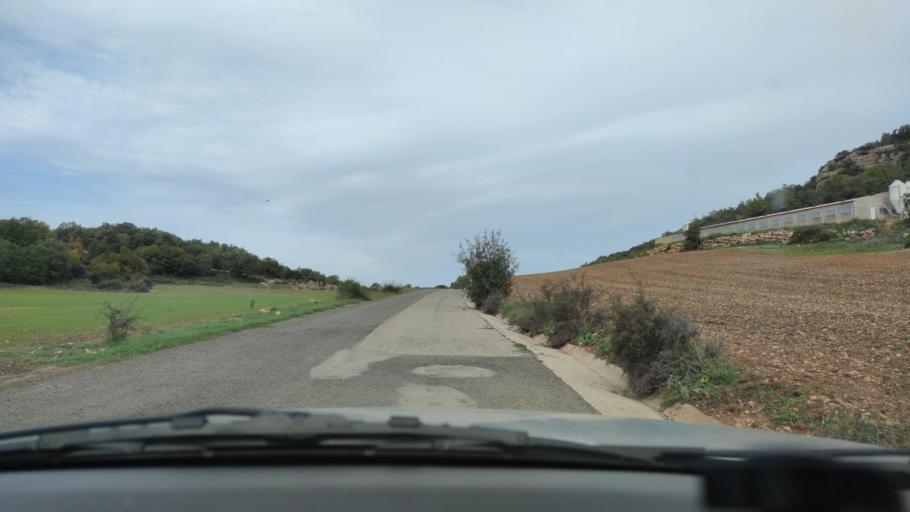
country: ES
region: Catalonia
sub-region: Provincia de Lleida
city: Llimiana
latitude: 42.0368
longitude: 1.0054
